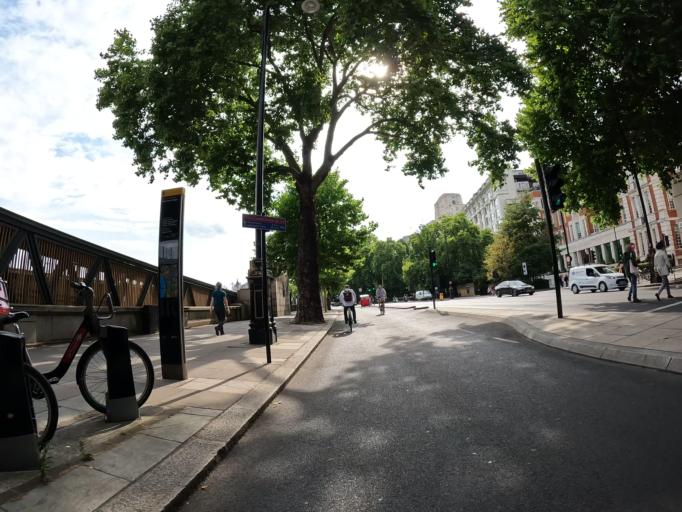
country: GB
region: England
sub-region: Greater London
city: Bethnal Green
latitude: 51.4966
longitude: -0.0611
